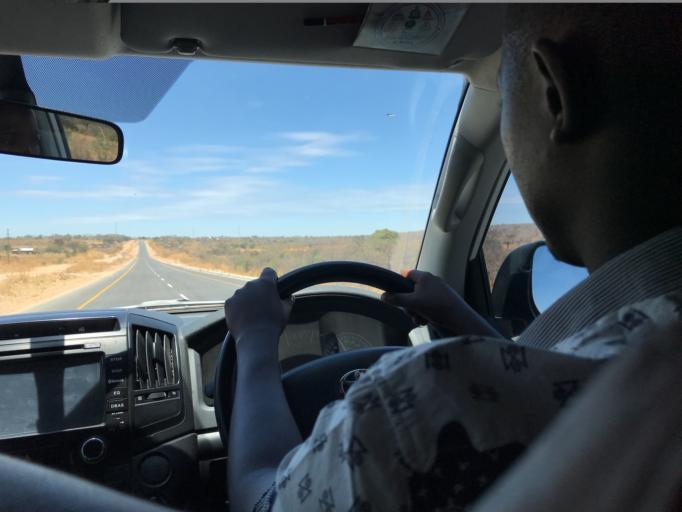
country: TZ
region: Njombe
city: Ilembula
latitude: -8.8463
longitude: 34.4746
